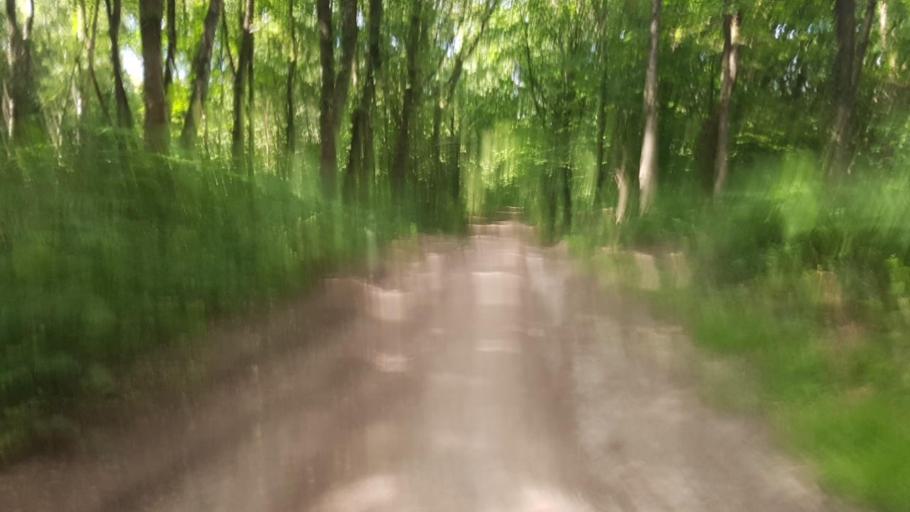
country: BE
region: Wallonia
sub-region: Province du Hainaut
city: Charleroi
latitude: 50.3623
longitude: 4.4516
